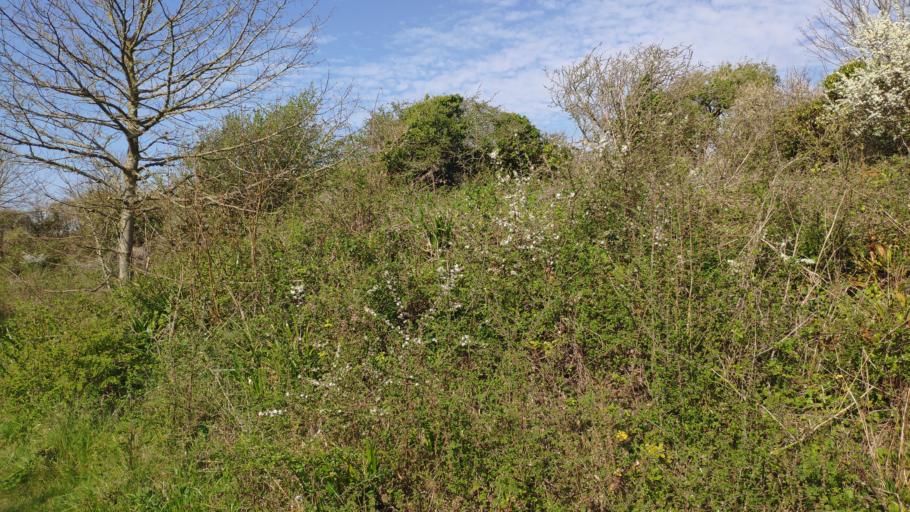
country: GB
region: England
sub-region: Dorset
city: Swanage
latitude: 50.6016
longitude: -1.9661
